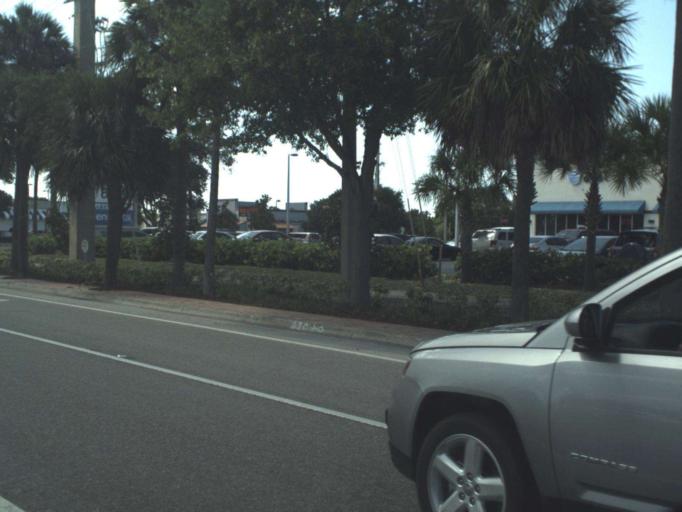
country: US
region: Florida
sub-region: Brevard County
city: Rockledge
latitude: 28.3573
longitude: -80.6828
